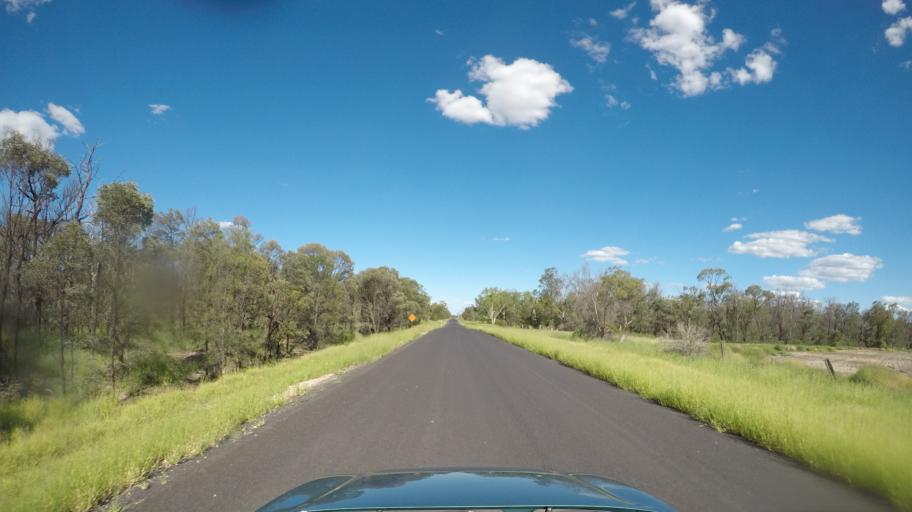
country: AU
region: Queensland
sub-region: Goondiwindi
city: Goondiwindi
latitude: -28.1666
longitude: 150.4452
